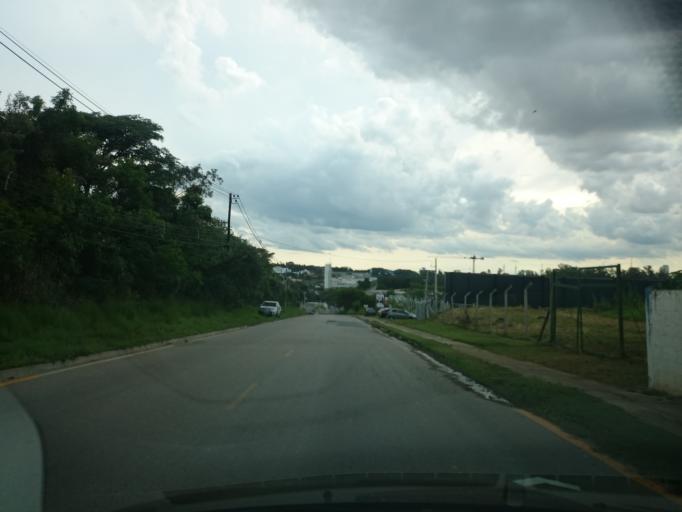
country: BR
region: Sao Paulo
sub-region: Sorocaba
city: Sorocaba
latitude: -23.4732
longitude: -47.4086
